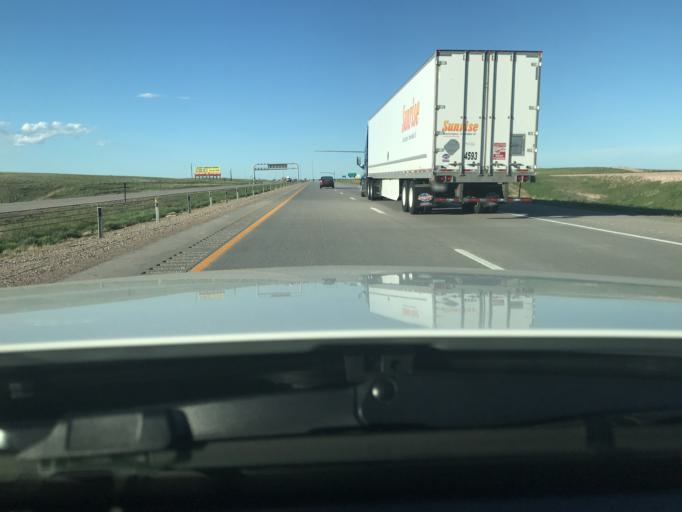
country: US
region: Wyoming
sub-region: Laramie County
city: South Greeley
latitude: 41.0716
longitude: -104.8639
